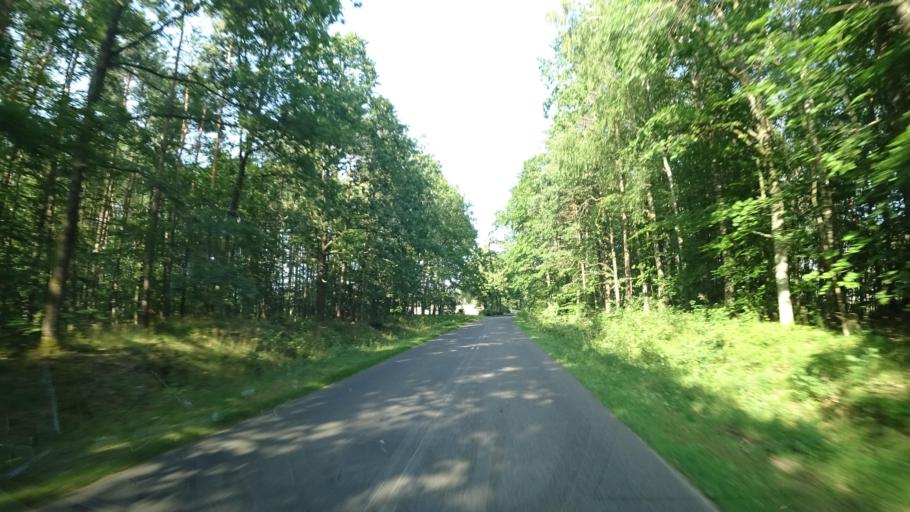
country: PL
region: Pomeranian Voivodeship
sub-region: Powiat czluchowski
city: Przechlewo
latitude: 53.7895
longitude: 17.2175
